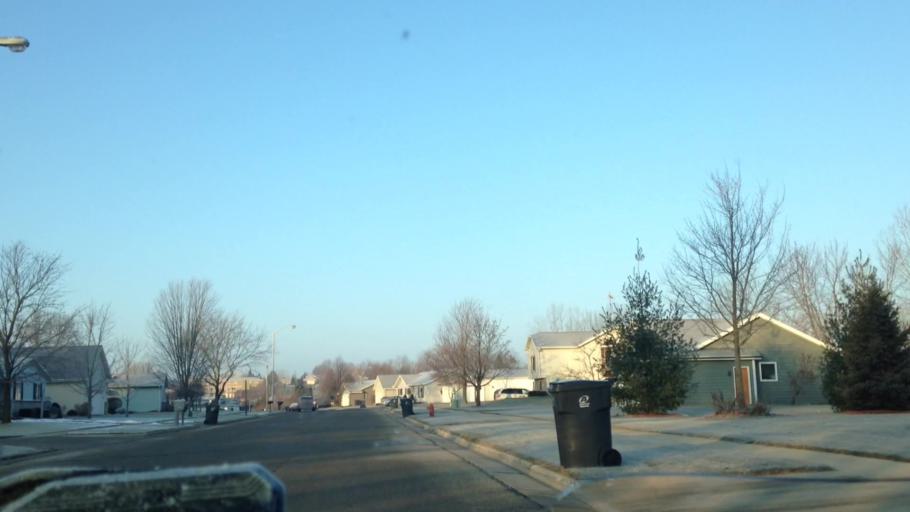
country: US
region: Wisconsin
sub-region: Dodge County
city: Mayville
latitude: 43.4977
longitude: -88.5585
